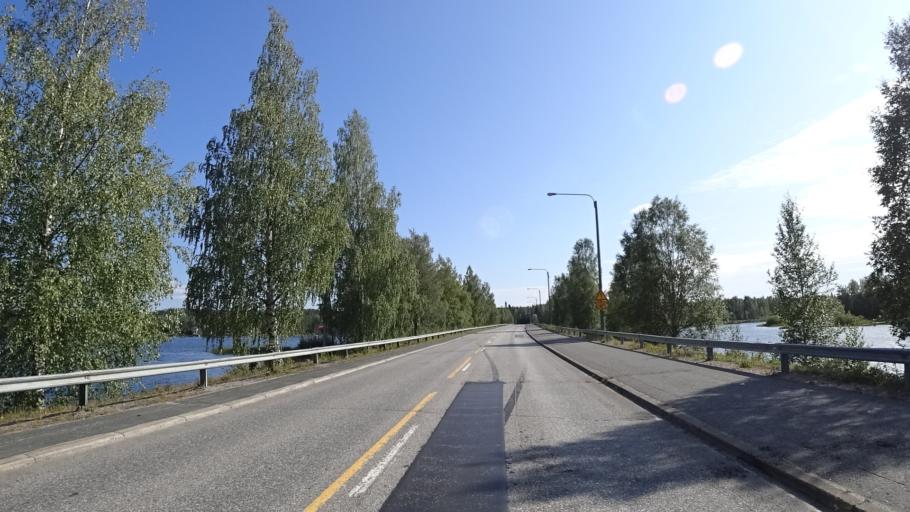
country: FI
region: North Karelia
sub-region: Joensuu
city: Eno
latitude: 62.8064
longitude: 30.1520
